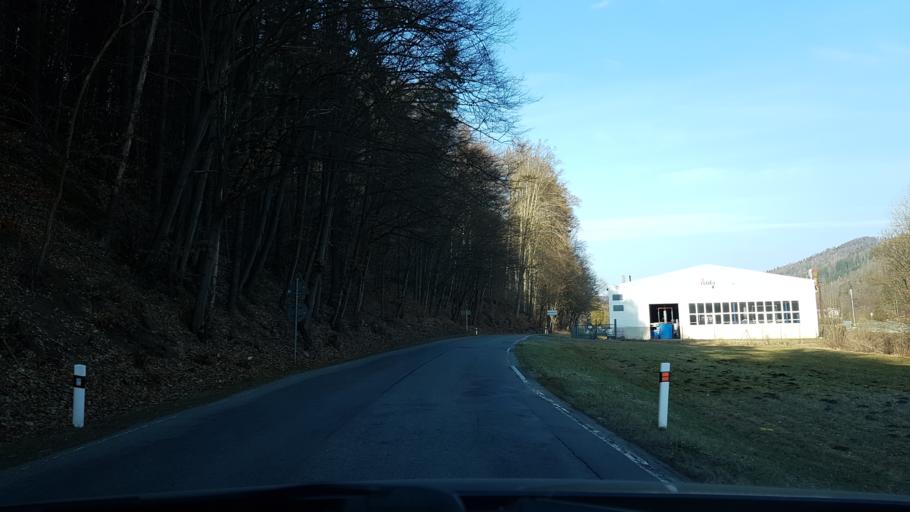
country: CZ
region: Olomoucky
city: Dolni Bohdikov
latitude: 50.0224
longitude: 16.8954
